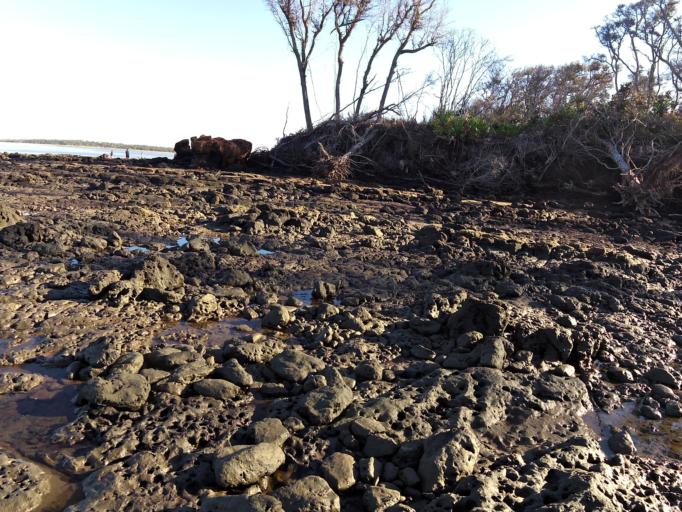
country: US
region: Florida
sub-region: Duval County
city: Atlantic Beach
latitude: 30.4938
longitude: -81.4378
